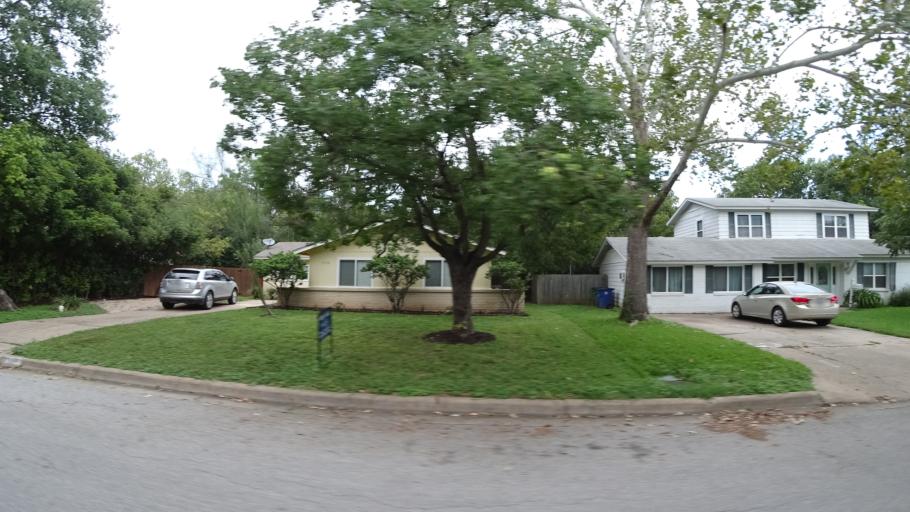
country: US
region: Texas
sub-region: Travis County
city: Rollingwood
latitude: 30.2175
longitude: -97.7934
